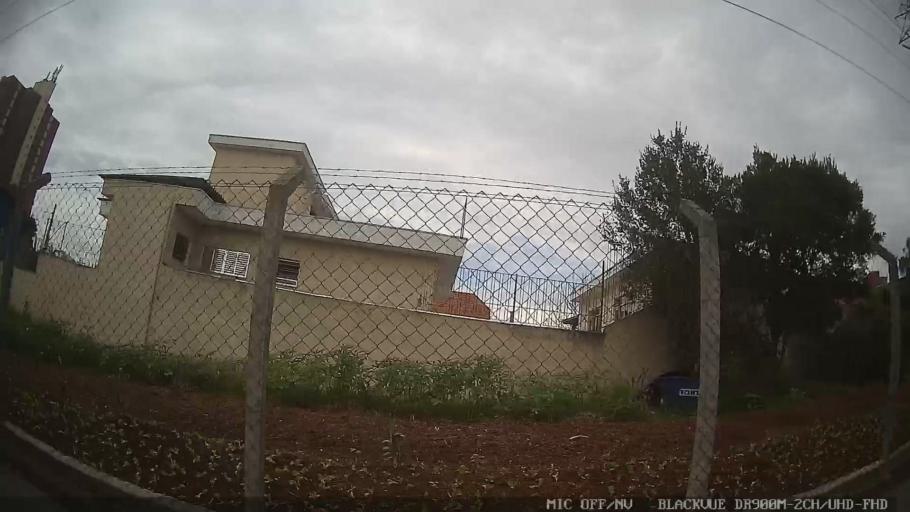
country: BR
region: Sao Paulo
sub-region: Maua
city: Maua
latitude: -23.6729
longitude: -46.4623
